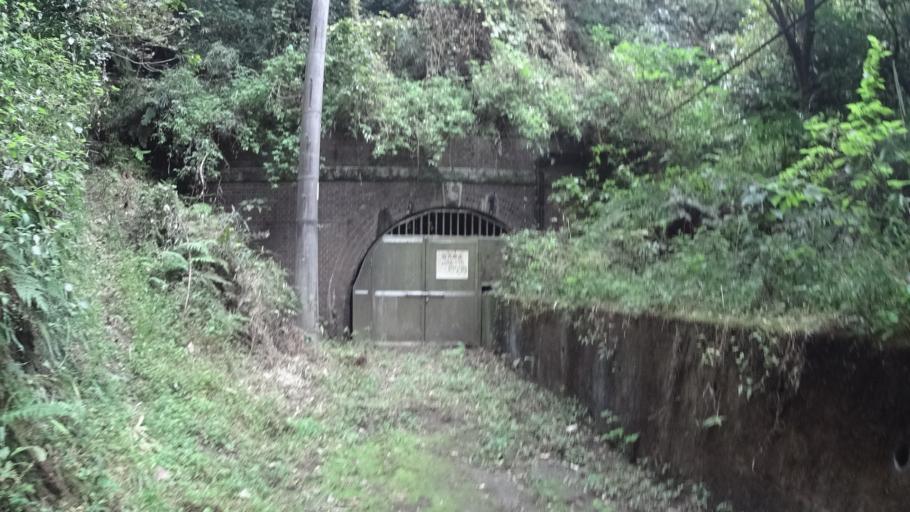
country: JP
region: Kanagawa
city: Zushi
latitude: 35.2936
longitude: 139.6213
